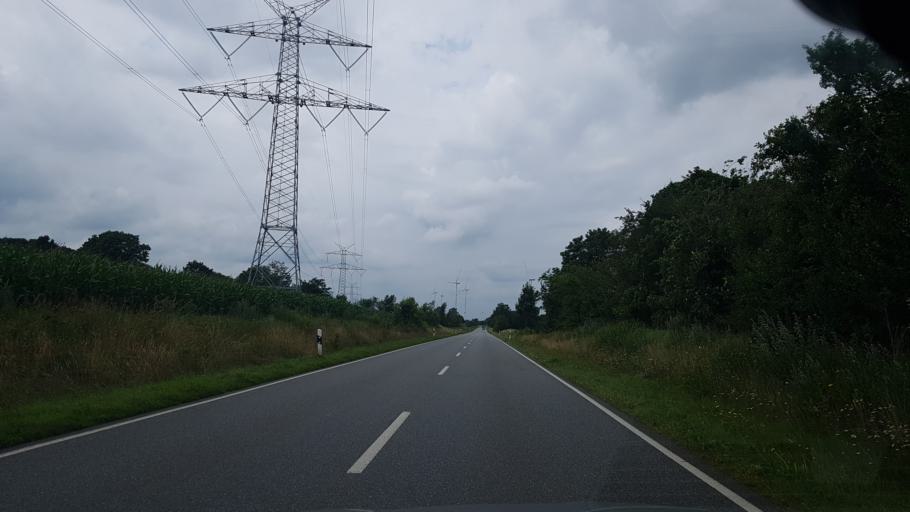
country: DE
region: Schleswig-Holstein
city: Jardelund
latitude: 54.8319
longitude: 9.2157
